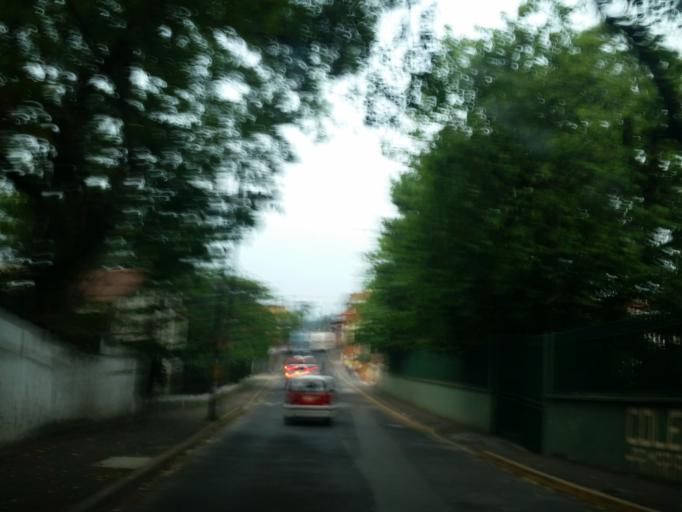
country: MX
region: Veracruz
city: Coatepec
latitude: 19.4574
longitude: -96.9524
